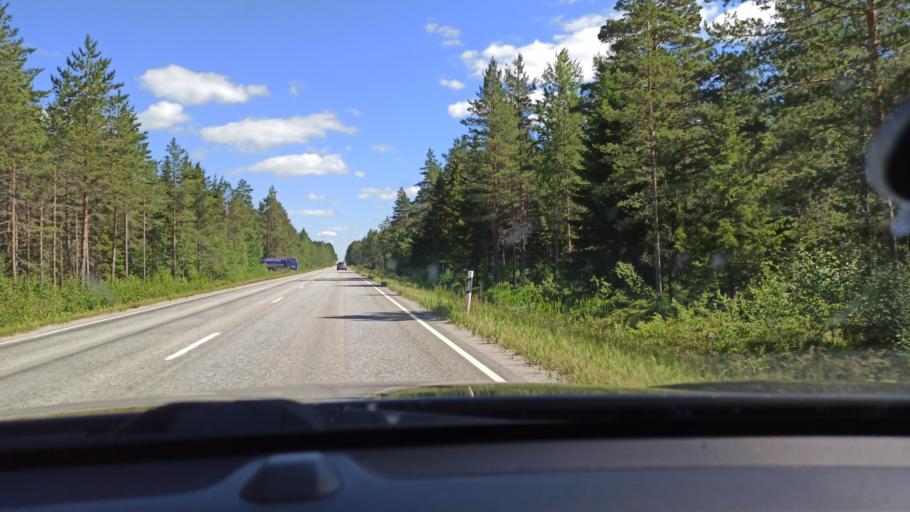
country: FI
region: Ostrobothnia
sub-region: Vaasa
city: Malax
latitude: 62.9768
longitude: 21.6080
